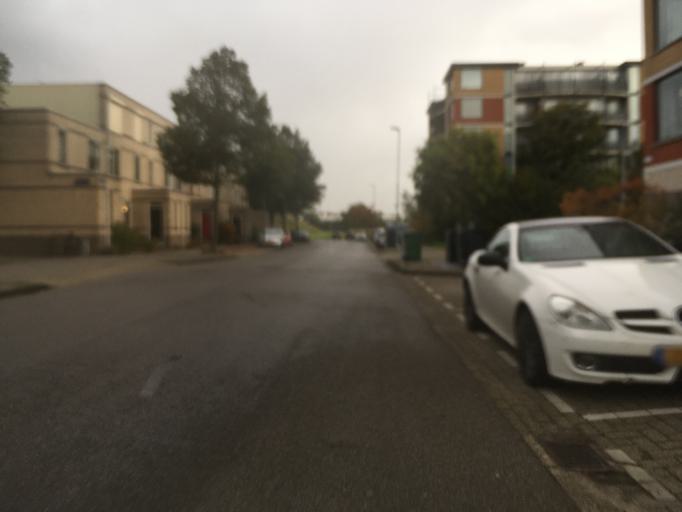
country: NL
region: North Holland
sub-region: Gemeente Haarlem
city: Haarlem
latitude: 52.3802
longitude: 4.6731
